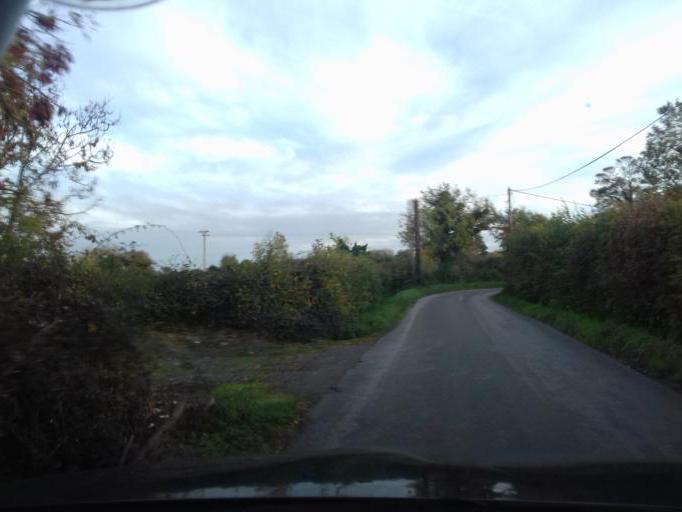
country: IE
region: Leinster
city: Hartstown
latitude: 53.3852
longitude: -6.4412
